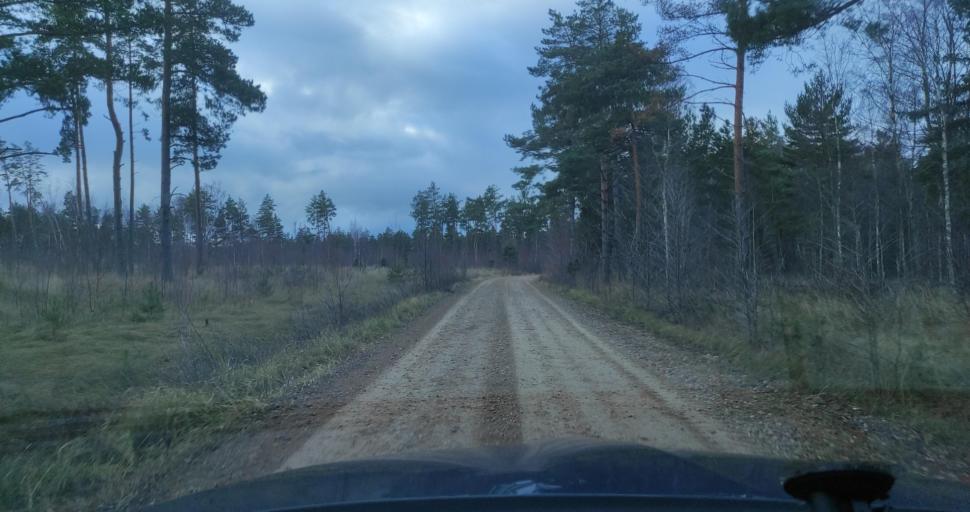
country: LV
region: Pavilostas
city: Pavilosta
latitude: 56.8199
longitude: 21.0655
